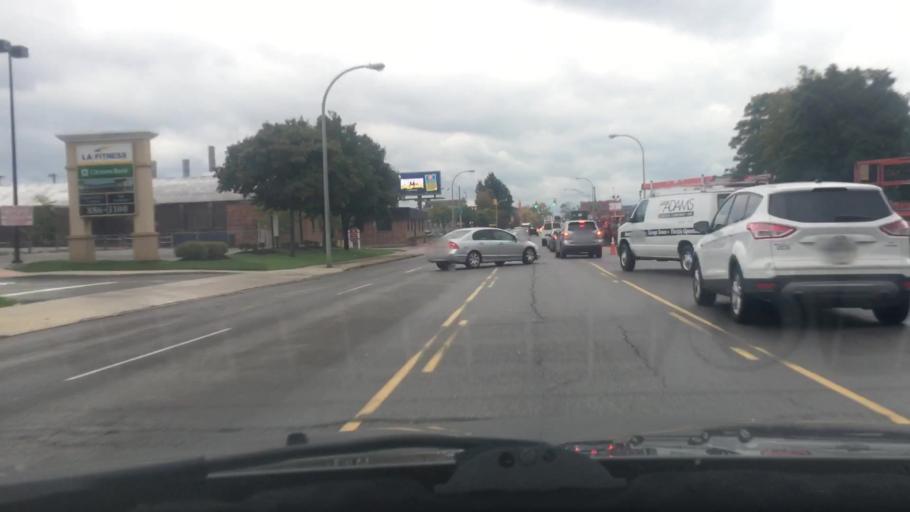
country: US
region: New York
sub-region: Erie County
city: Kenmore
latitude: 42.9493
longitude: -78.8783
